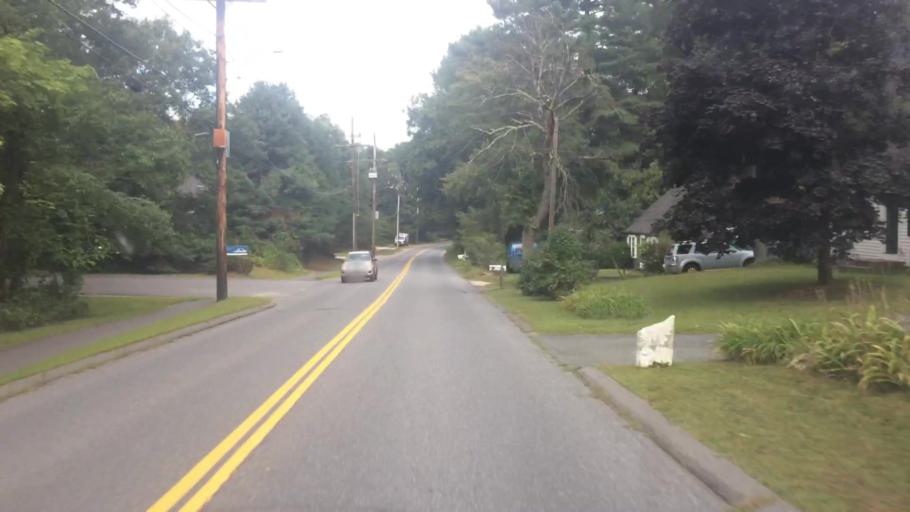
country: US
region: Massachusetts
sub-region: Middlesex County
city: West Concord
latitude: 42.4605
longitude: -71.4163
